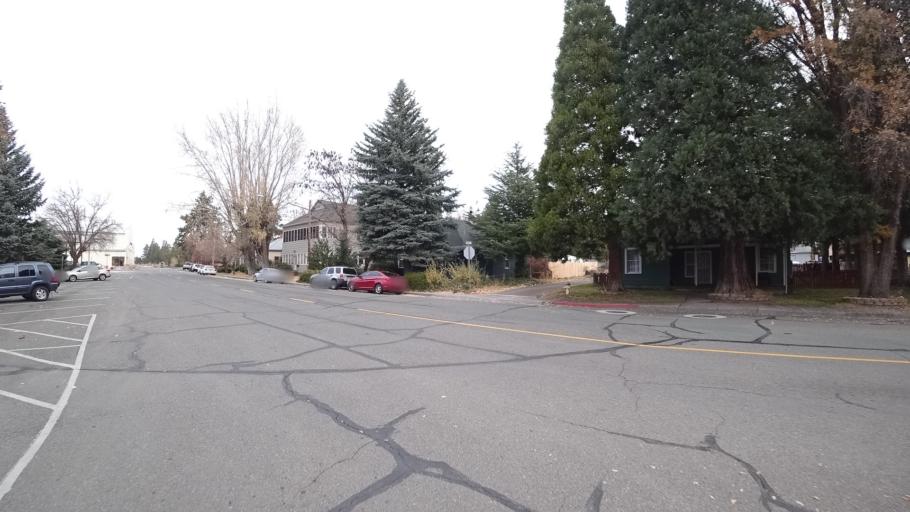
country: US
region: California
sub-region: Siskiyou County
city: Weed
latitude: 41.4270
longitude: -122.3843
